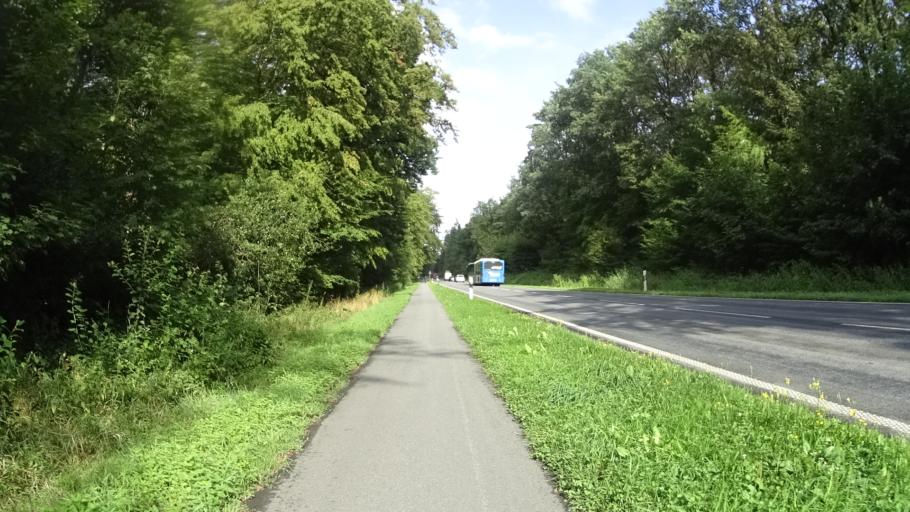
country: DE
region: Lower Saxony
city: Bockhorn
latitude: 53.3843
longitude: 8.0654
